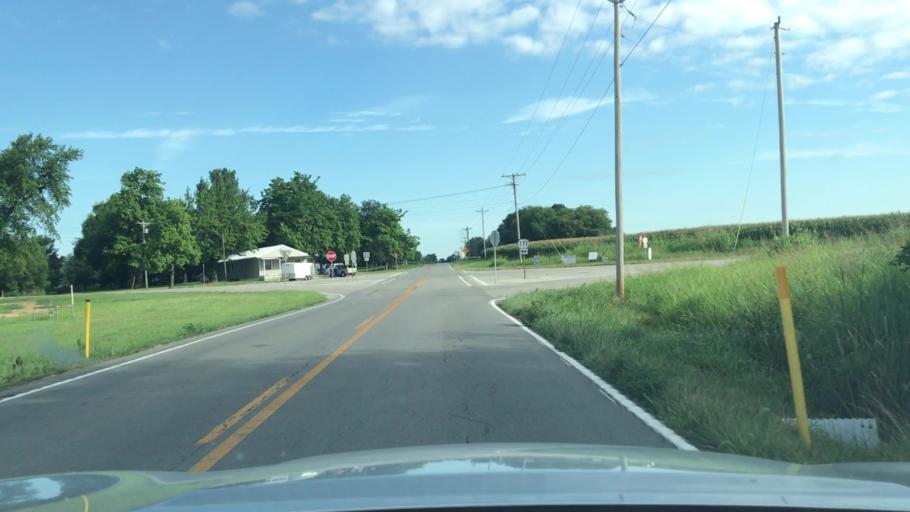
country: US
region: Kentucky
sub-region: Todd County
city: Elkton
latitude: 36.8662
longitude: -87.1625
